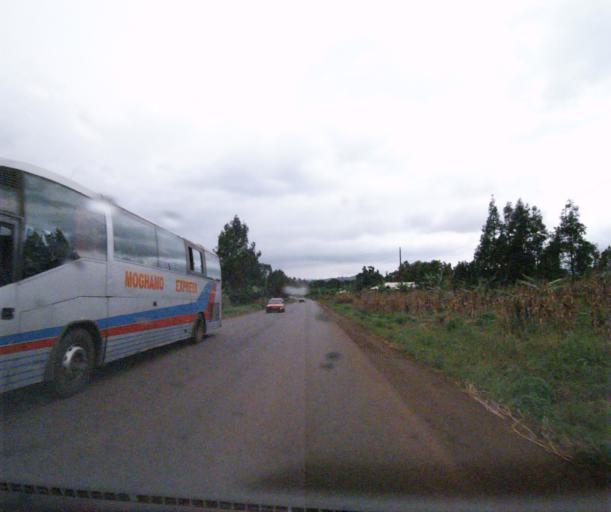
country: CM
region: West
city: Bansoa
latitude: 5.4895
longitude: 10.2004
